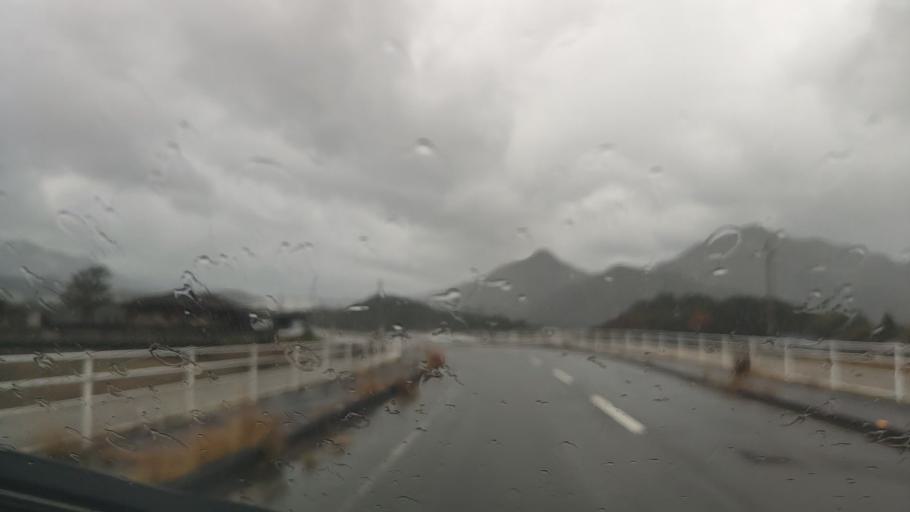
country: JP
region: Tokushima
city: Kamojimacho-jogejima
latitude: 34.2089
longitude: 134.3413
